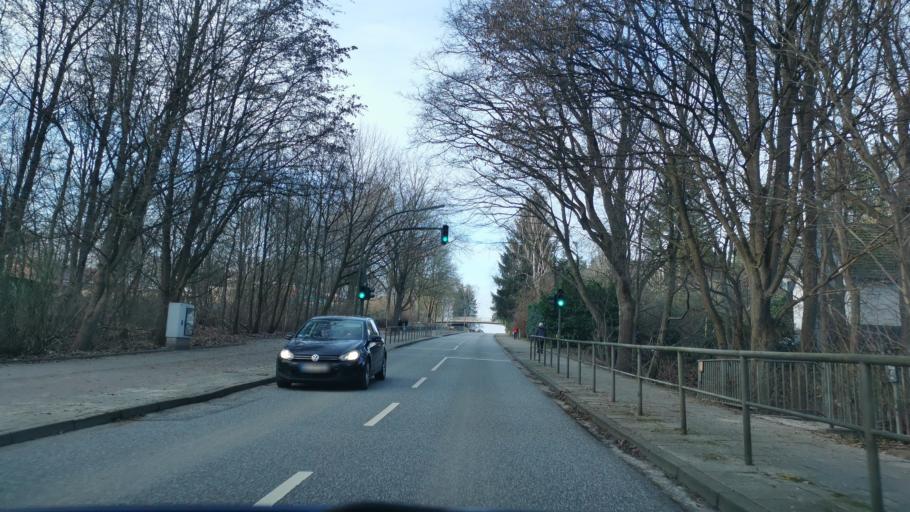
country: DE
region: Lower Saxony
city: Seevetal
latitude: 53.4296
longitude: 9.9720
